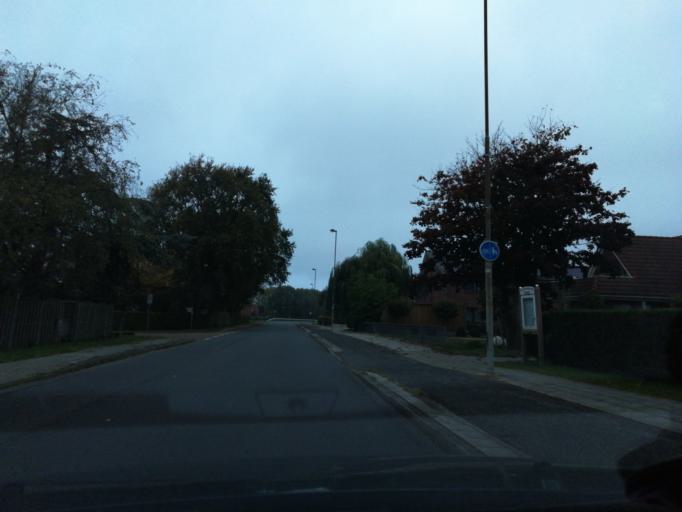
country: DE
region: Lower Saxony
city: Werdum
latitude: 53.6930
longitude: 7.8064
